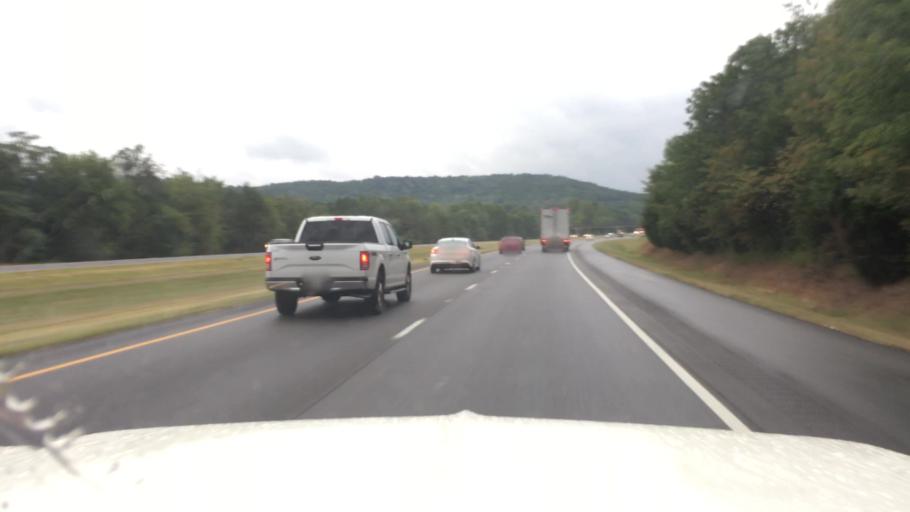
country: US
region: Alabama
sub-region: Morgan County
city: Falkville
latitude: 34.3438
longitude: -86.8927
